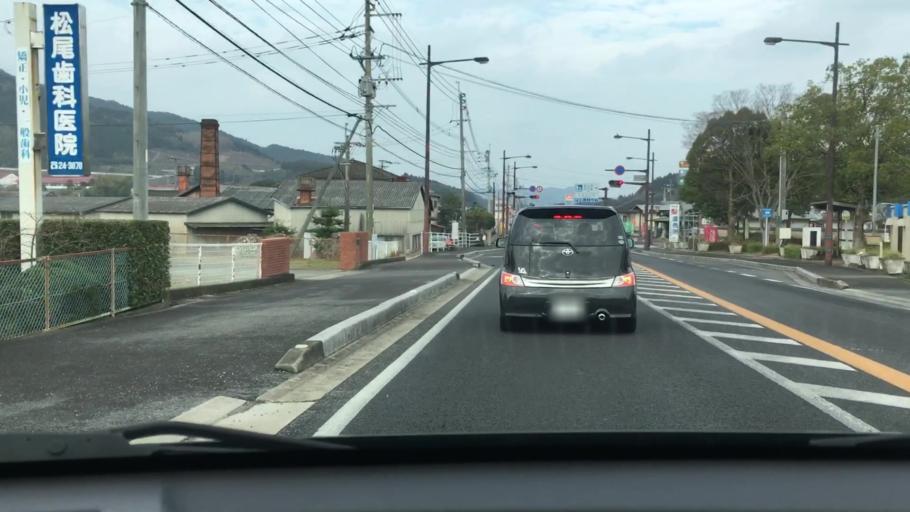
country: JP
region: Saga Prefecture
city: Imaricho-ko
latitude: 33.3126
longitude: 129.9285
